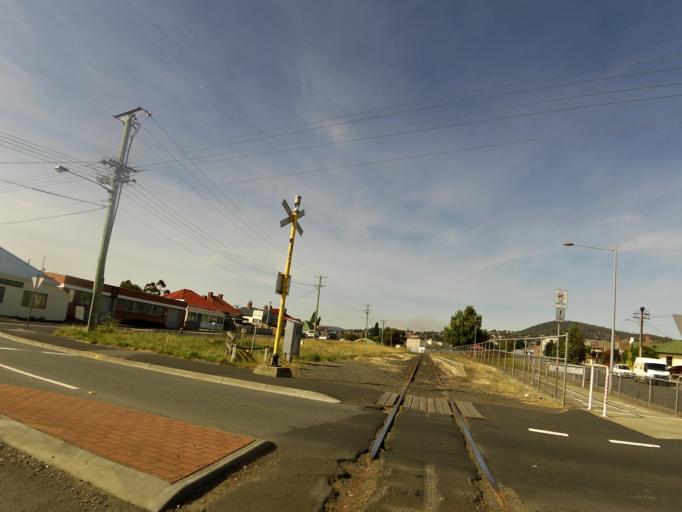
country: AU
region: Tasmania
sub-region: Glenorchy
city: Moonah
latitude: -42.8476
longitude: 147.2984
